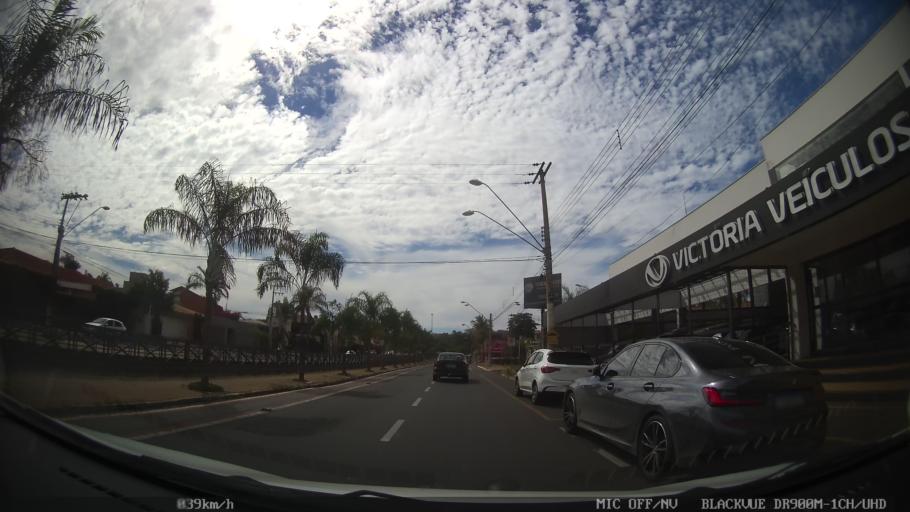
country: BR
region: Sao Paulo
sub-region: Catanduva
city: Catanduva
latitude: -21.1403
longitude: -48.9678
